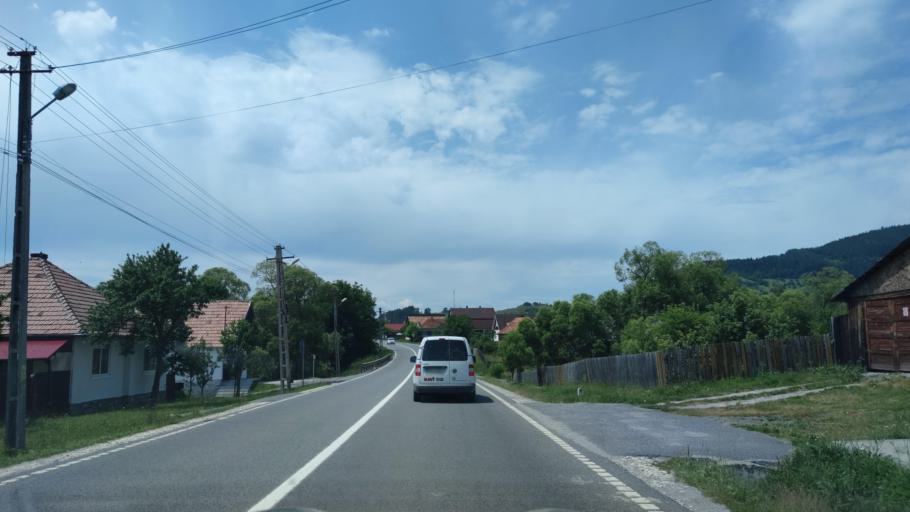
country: RO
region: Harghita
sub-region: Comuna Voslobeni
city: Voslobeni
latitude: 46.6269
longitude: 25.6608
